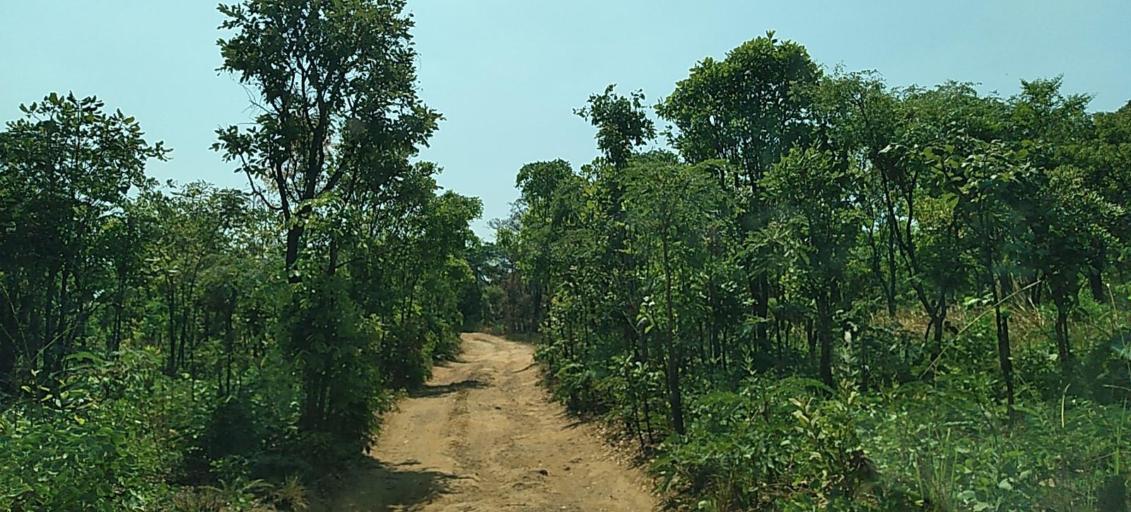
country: ZM
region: North-Western
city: Solwezi
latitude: -12.0986
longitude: 26.2800
